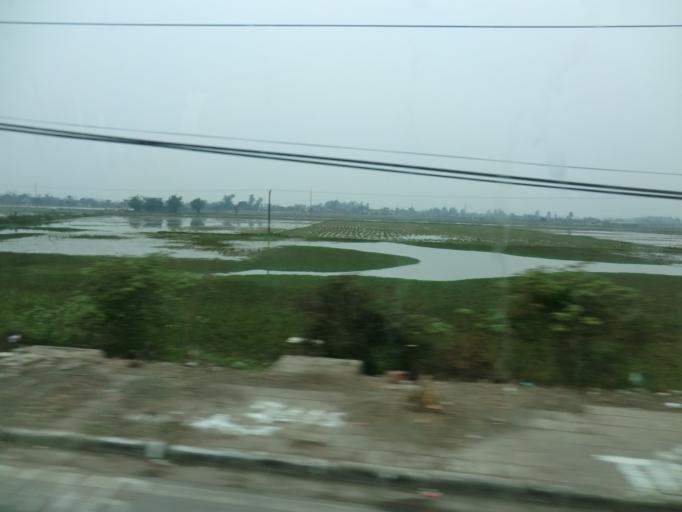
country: VN
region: Nam Dinh
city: Thi Tran Goi
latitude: 20.3277
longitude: 106.0674
